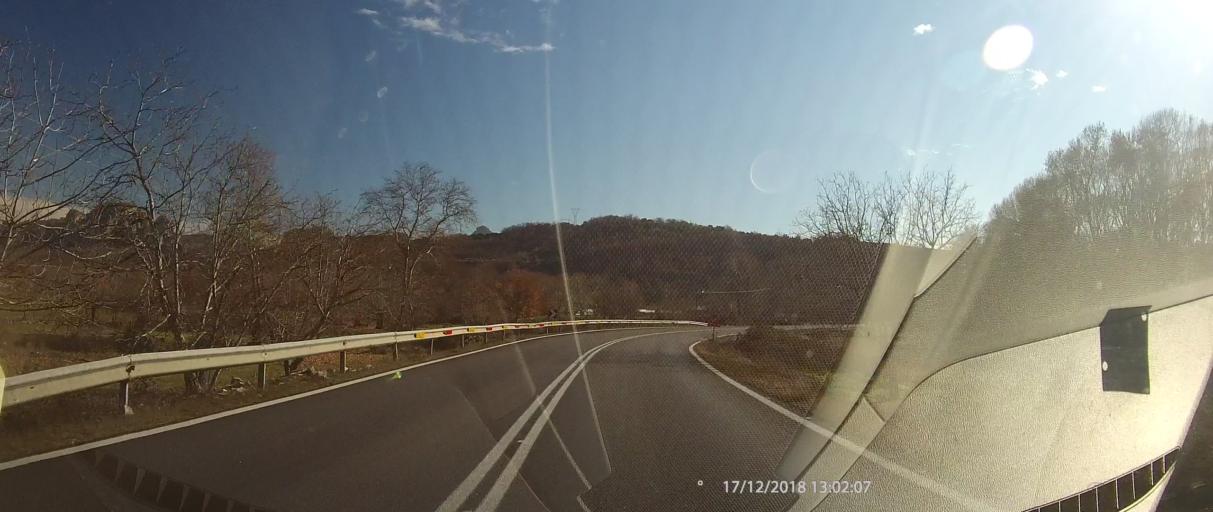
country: GR
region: Thessaly
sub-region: Trikala
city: Kastraki
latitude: 39.7279
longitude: 21.5926
